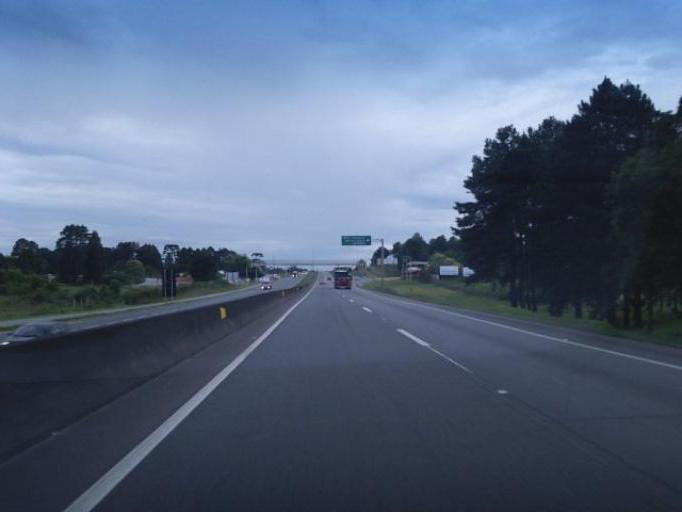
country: BR
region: Parana
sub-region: Sao Jose Dos Pinhais
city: Sao Jose dos Pinhais
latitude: -25.6600
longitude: -49.1553
